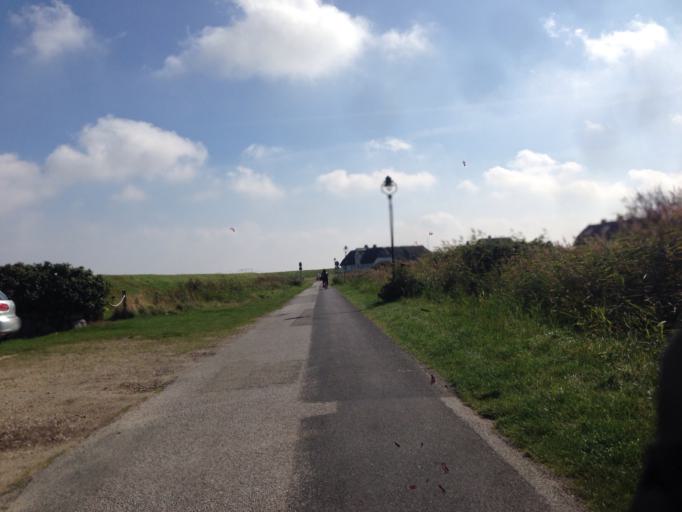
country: DE
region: Schleswig-Holstein
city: Westerland
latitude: 54.8472
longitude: 8.2951
